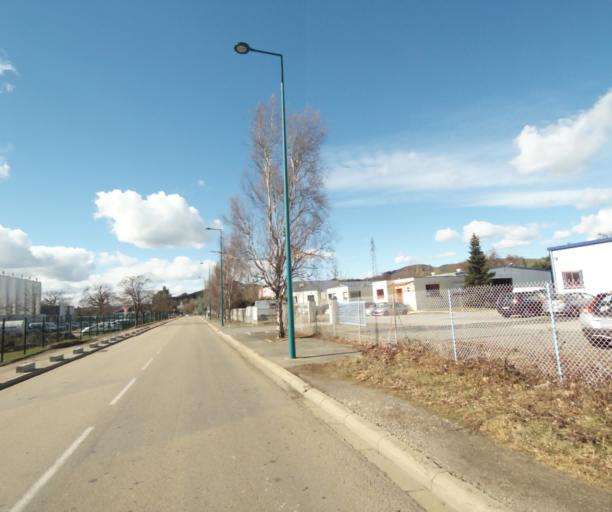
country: FR
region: Rhone-Alpes
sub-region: Departement de la Loire
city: La Talaudiere
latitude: 45.4744
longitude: 4.4302
